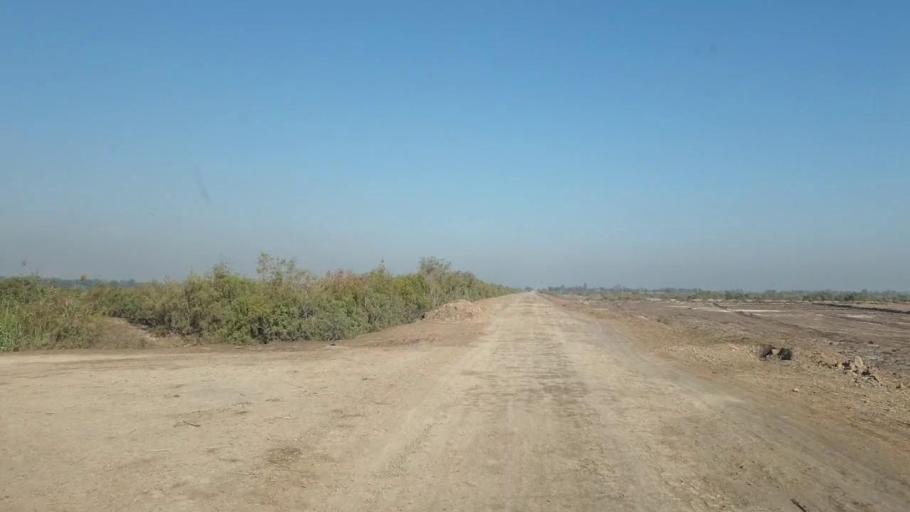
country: PK
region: Sindh
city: Shahdadpur
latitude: 25.9830
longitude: 68.4959
